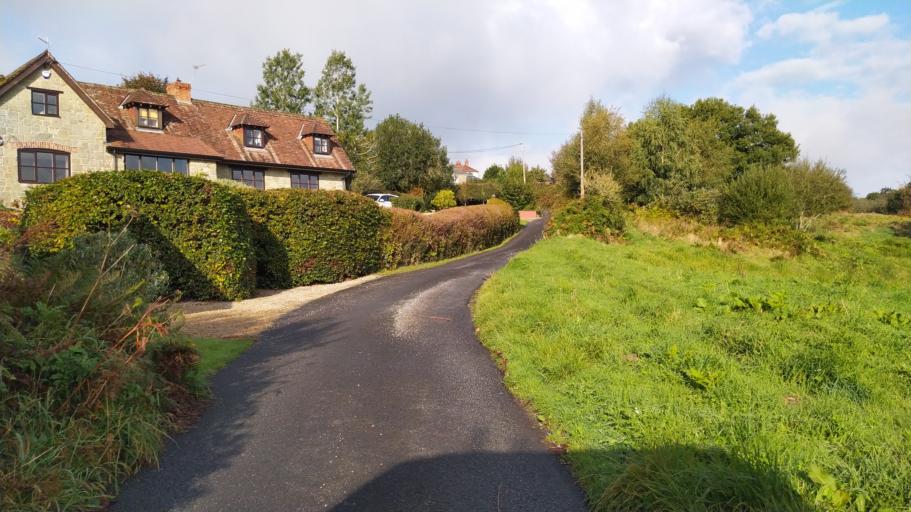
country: GB
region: England
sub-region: Dorset
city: Shaftesbury
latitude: 51.0301
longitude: -2.1467
